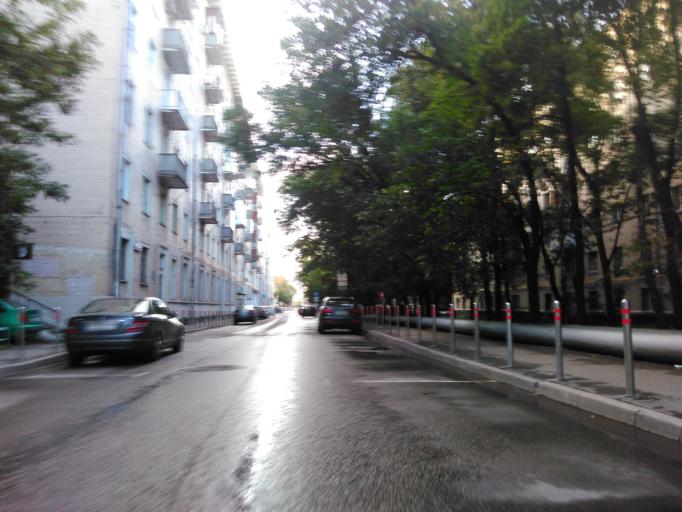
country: RU
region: Moscow
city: Taganskiy
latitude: 55.7565
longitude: 37.6538
